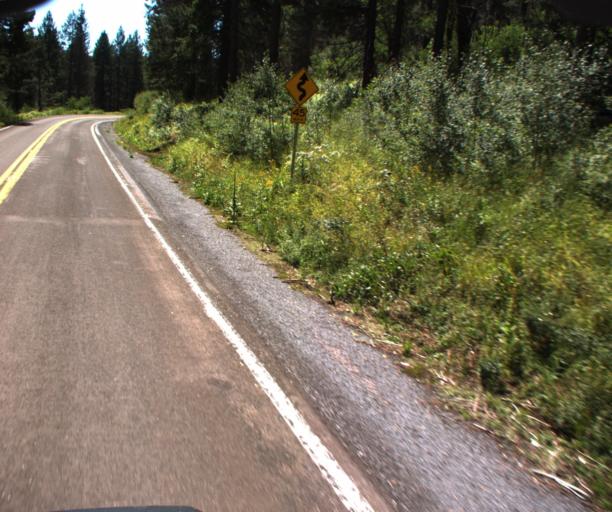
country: US
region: Arizona
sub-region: Greenlee County
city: Morenci
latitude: 33.5771
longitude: -109.3606
